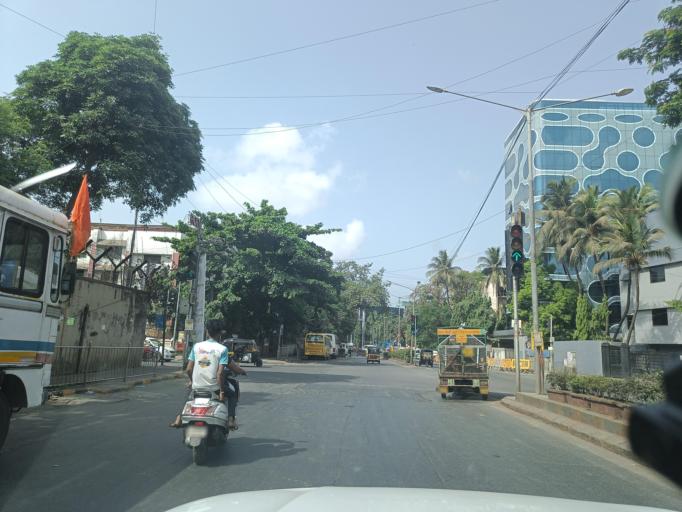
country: IN
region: Maharashtra
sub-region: Mumbai Suburban
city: Powai
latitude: 19.1234
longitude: 72.8717
